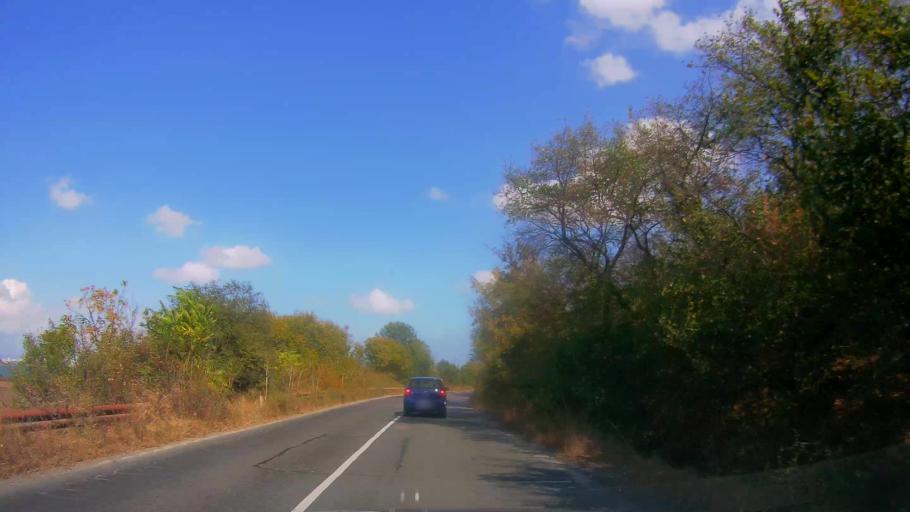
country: BG
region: Burgas
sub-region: Obshtina Burgas
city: Burgas
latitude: 42.4772
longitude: 27.4070
